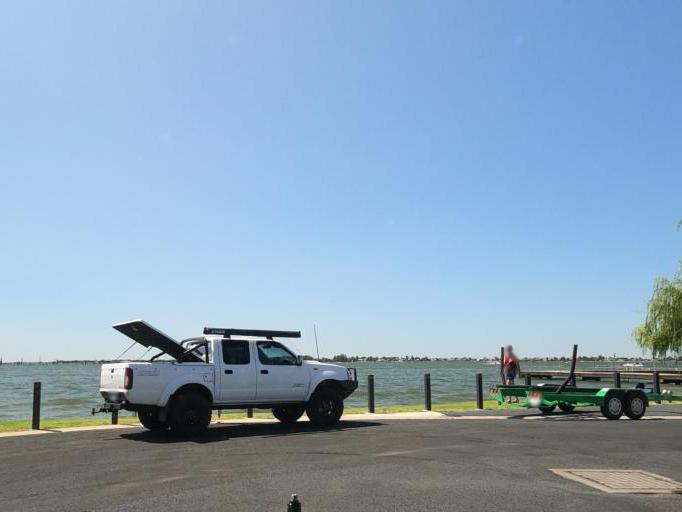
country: AU
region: New South Wales
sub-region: Corowa Shire
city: Mulwala
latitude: -35.9883
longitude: 146.0072
